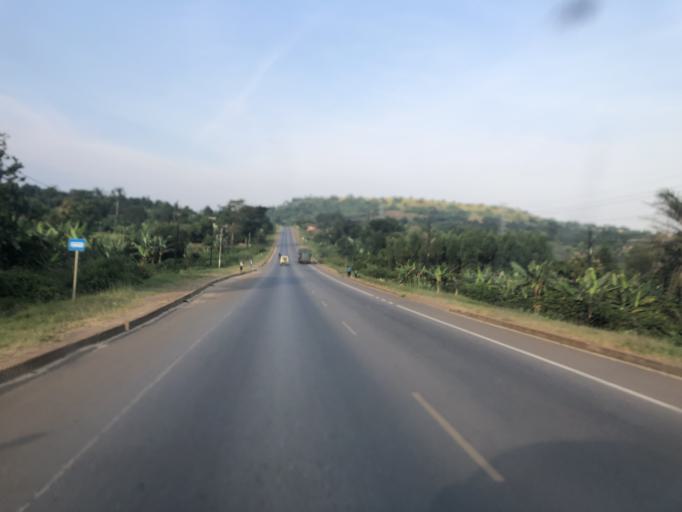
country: UG
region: Central Region
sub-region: Mpigi District
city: Mpigi
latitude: 0.1725
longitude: 32.2669
